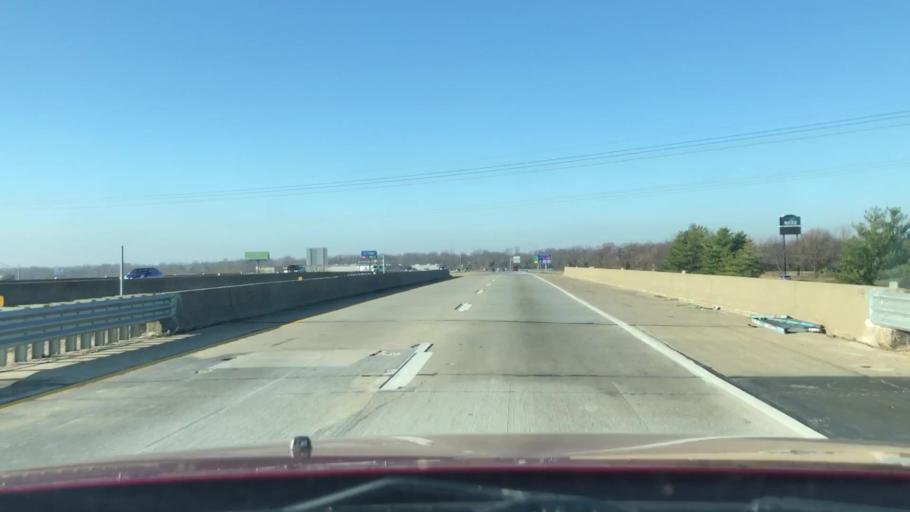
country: US
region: Missouri
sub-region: Greene County
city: Battlefield
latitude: 37.1359
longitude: -93.2960
